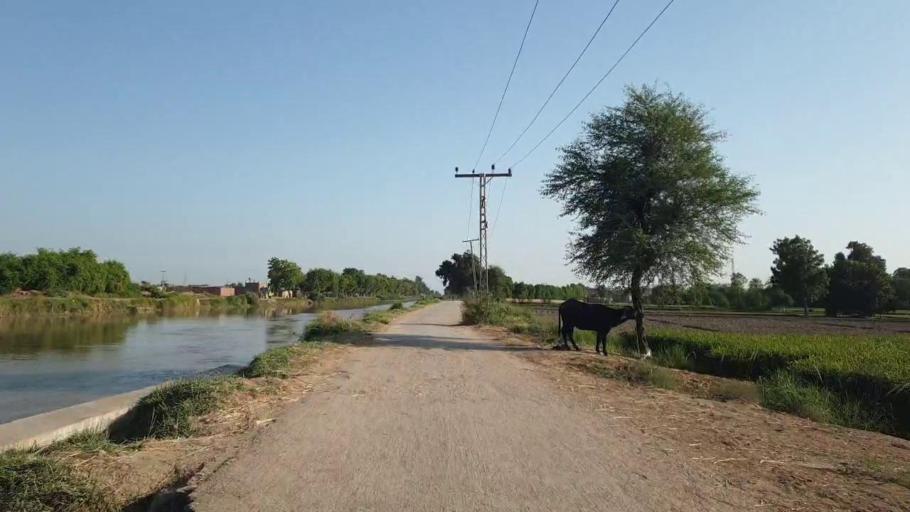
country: PK
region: Sindh
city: Hyderabad
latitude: 25.3219
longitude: 68.4273
